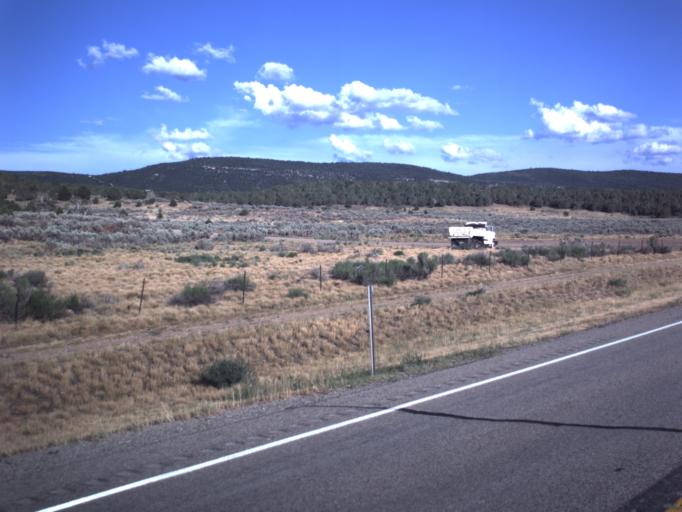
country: US
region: Utah
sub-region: Sanpete County
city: Fairview
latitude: 39.7681
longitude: -111.4862
